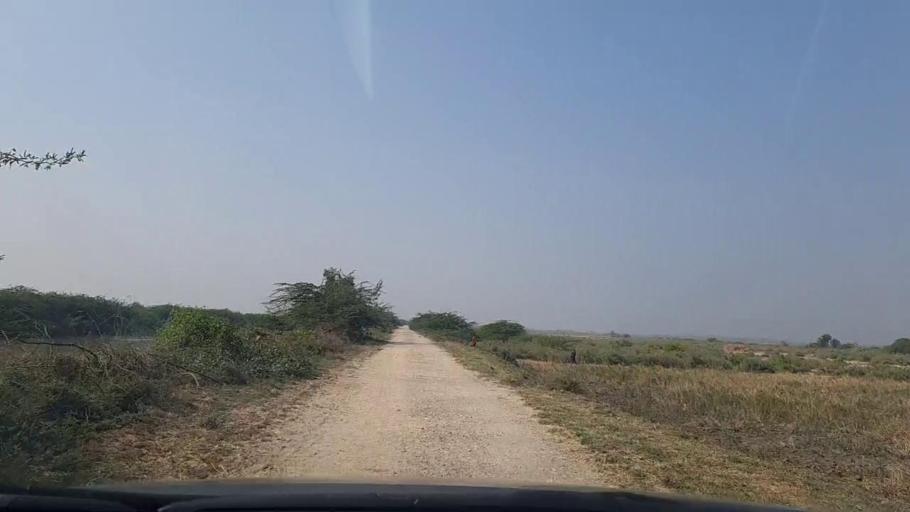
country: PK
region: Sindh
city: Mirpur Sakro
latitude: 24.5749
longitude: 67.7710
